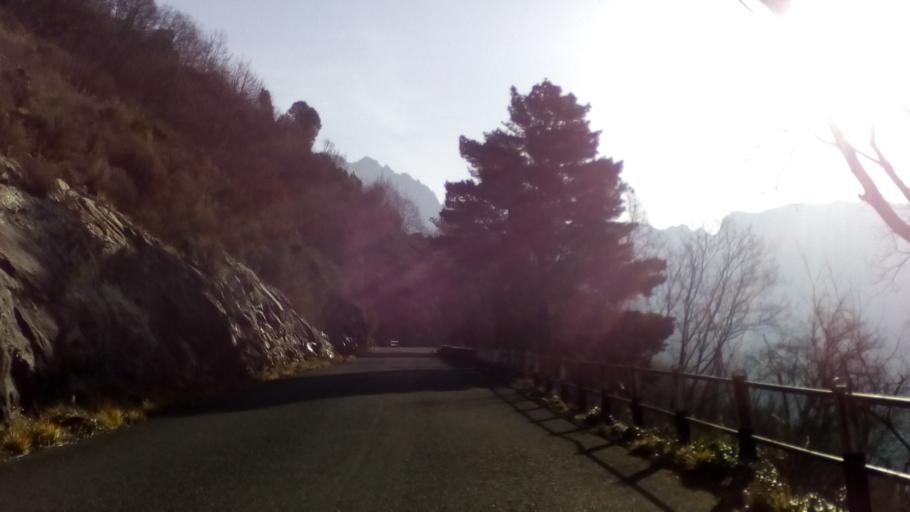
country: IT
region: Tuscany
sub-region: Provincia di Massa-Carrara
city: Montignoso
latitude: 44.0582
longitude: 10.1873
